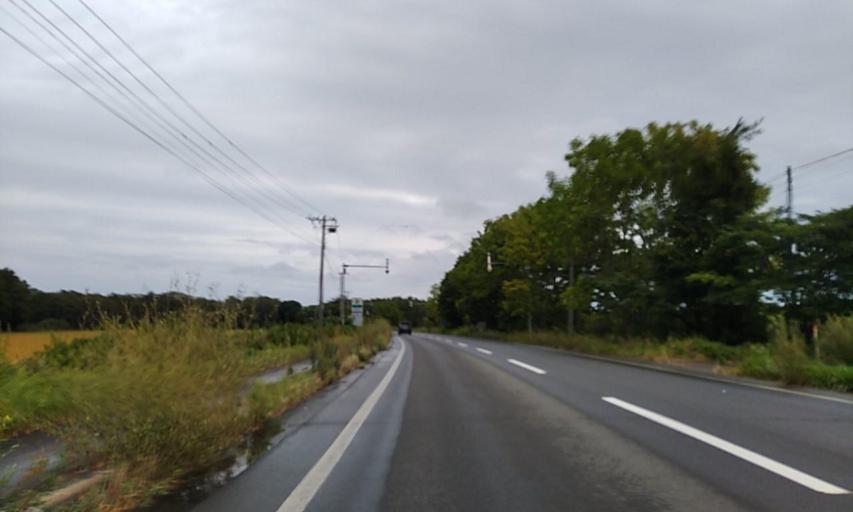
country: JP
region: Hokkaido
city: Kitami
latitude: 44.0886
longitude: 143.9539
